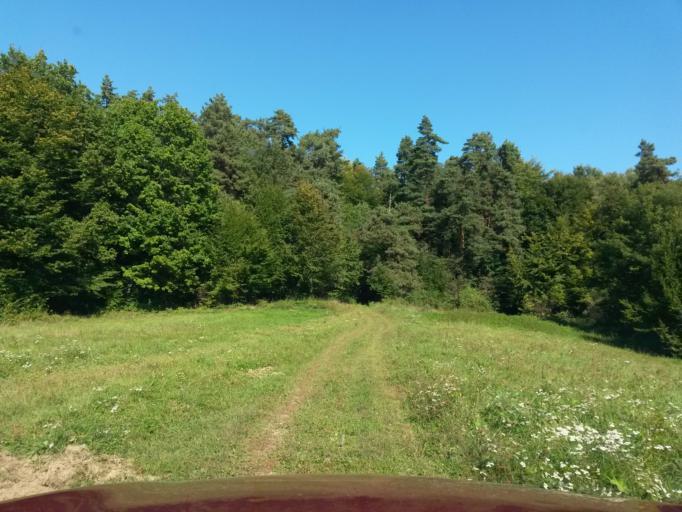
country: SK
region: Presovsky
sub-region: Okres Presov
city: Presov
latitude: 48.9806
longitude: 21.1481
